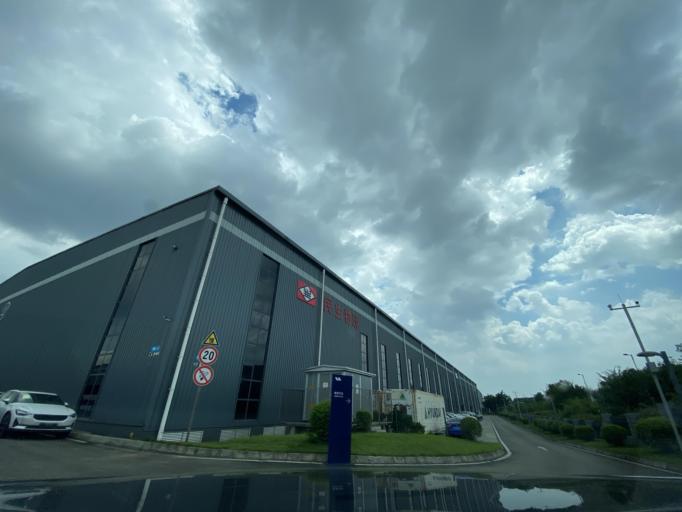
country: CN
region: Sichuan
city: Longquan
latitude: 30.5324
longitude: 104.1959
